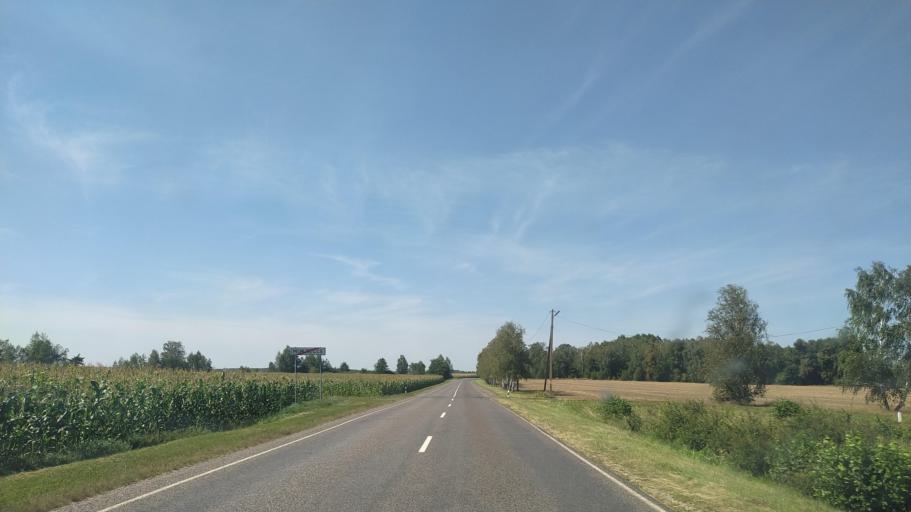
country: BY
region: Brest
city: Byaroza
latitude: 52.3934
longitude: 25.0116
